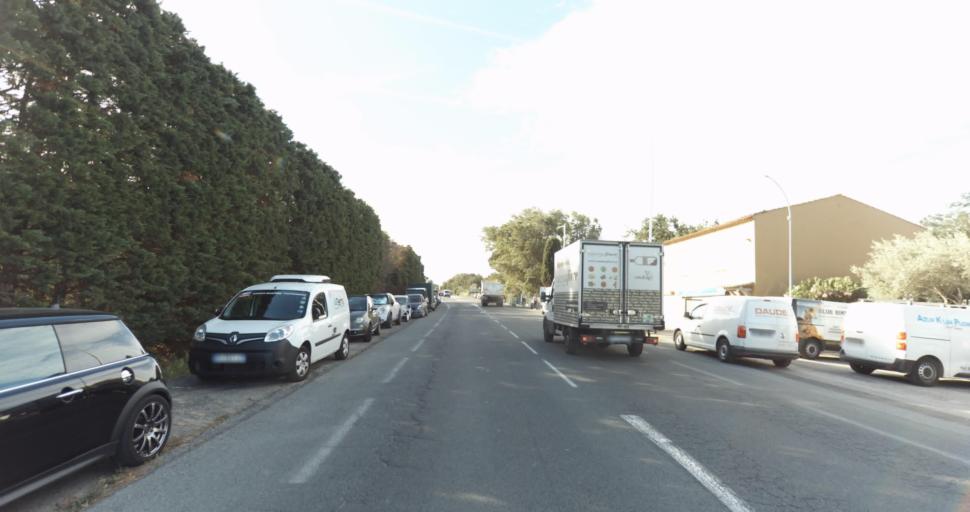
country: FR
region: Provence-Alpes-Cote d'Azur
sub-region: Departement du Var
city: Saint-Tropez
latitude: 43.2577
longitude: 6.6337
